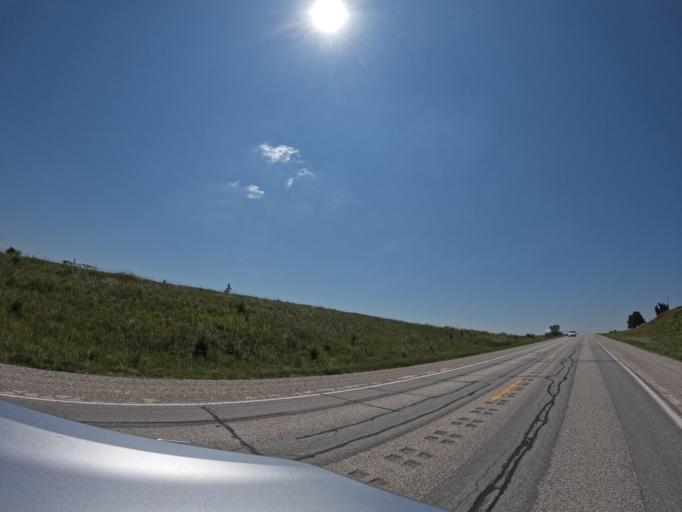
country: US
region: Iowa
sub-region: Keokuk County
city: Sigourney
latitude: 41.2782
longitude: -92.2043
